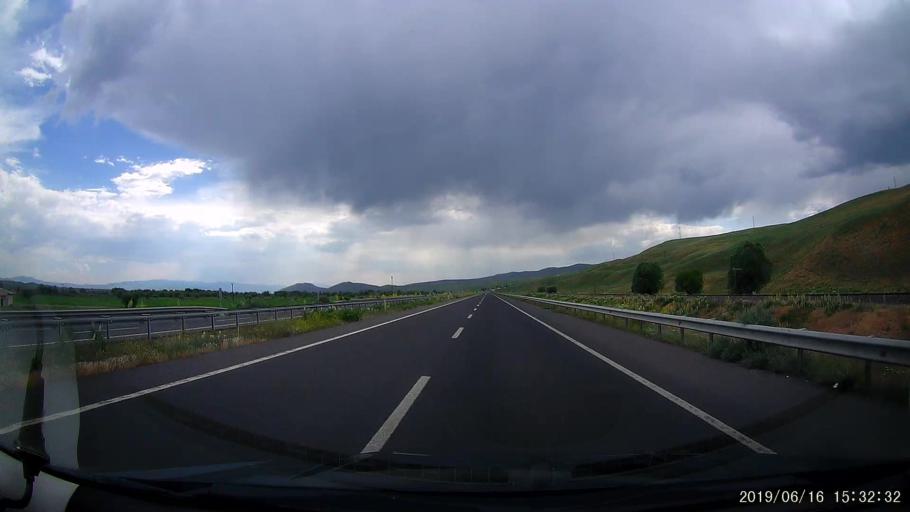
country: TR
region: Erzurum
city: Horasan
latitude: 40.0295
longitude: 42.0446
